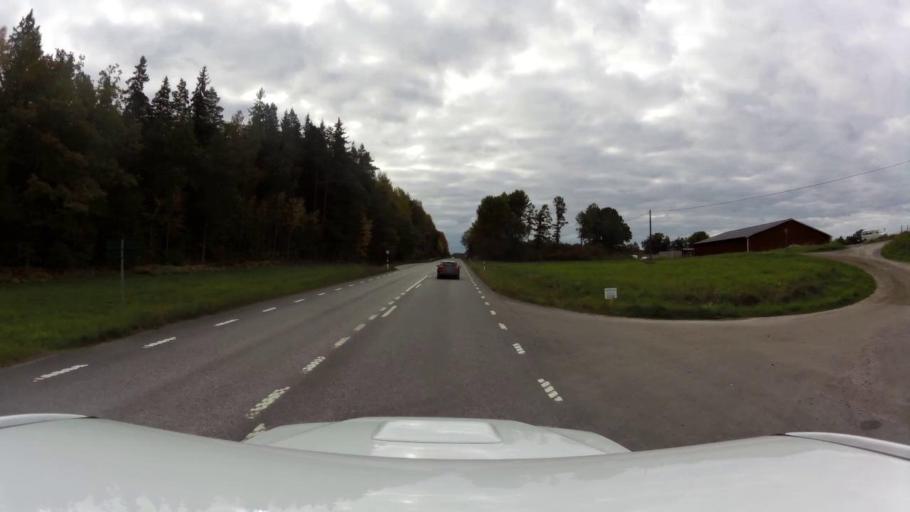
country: SE
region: OEstergoetland
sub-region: Kinda Kommun
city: Rimforsa
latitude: 58.1801
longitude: 15.6739
